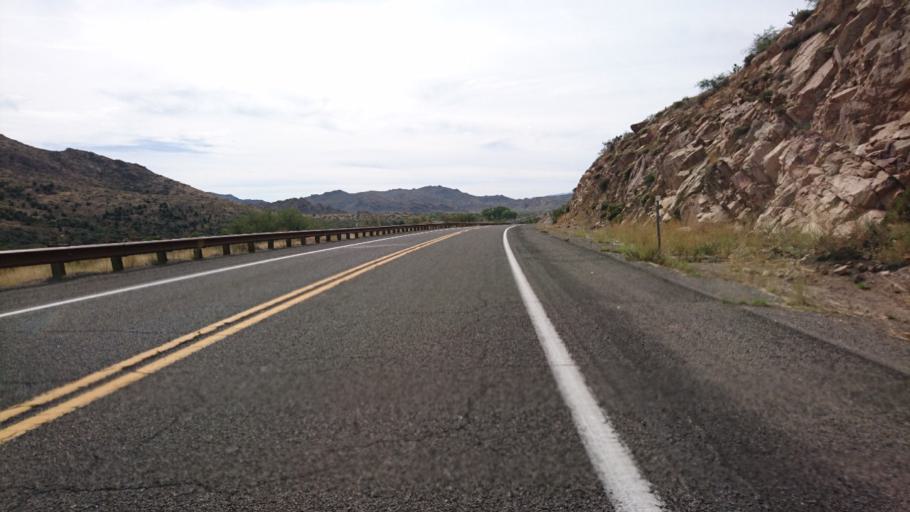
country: US
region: Arizona
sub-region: Mohave County
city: Peach Springs
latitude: 35.3933
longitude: -113.6557
